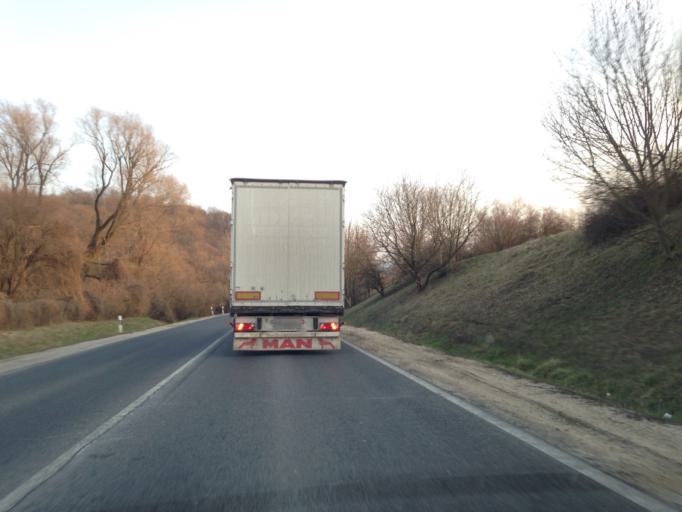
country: HU
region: Komarom-Esztergom
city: Tatabanya
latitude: 47.5720
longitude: 18.4375
